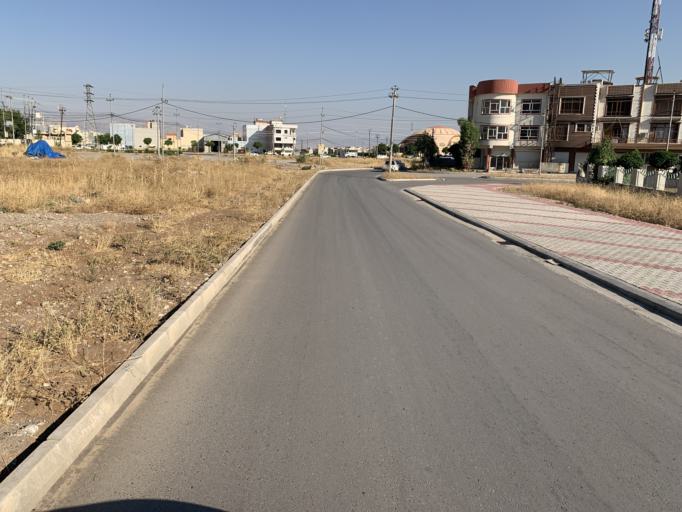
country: IQ
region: As Sulaymaniyah
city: Raniye
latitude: 36.2397
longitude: 44.8711
